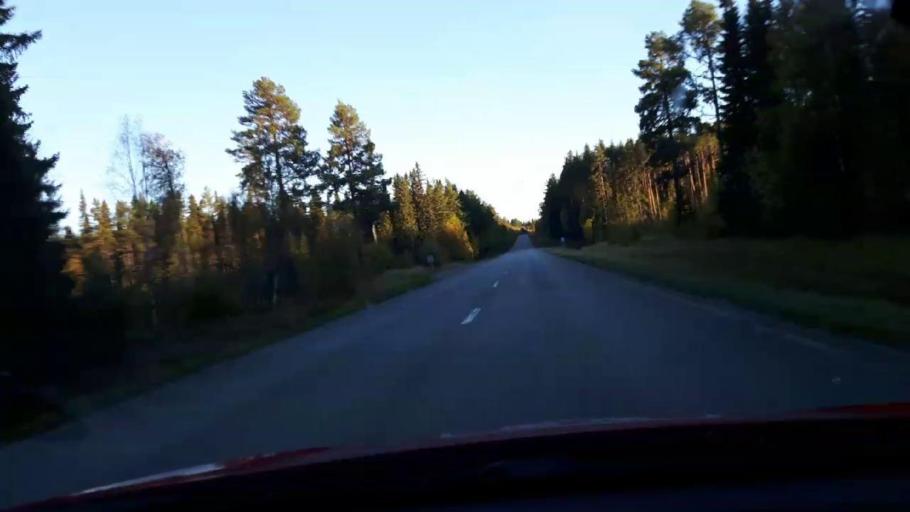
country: SE
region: Jaemtland
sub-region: Krokoms Kommun
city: Krokom
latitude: 63.4434
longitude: 14.4941
